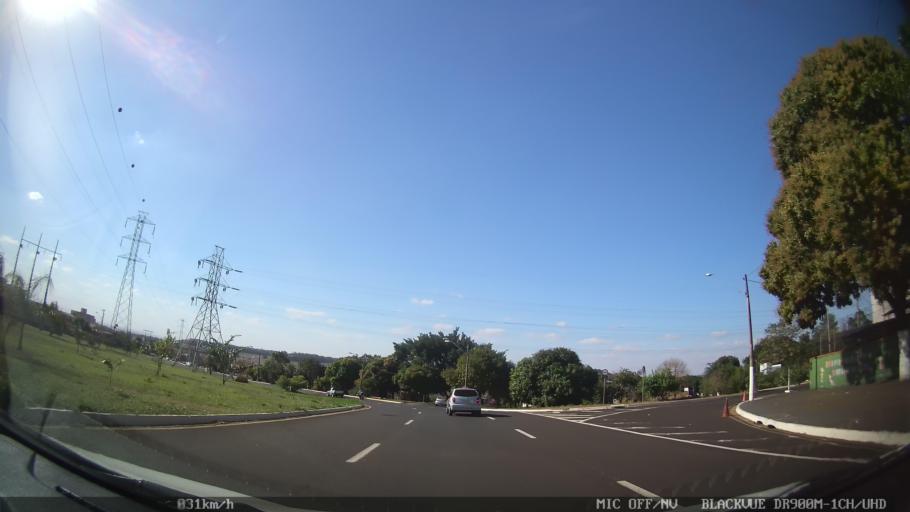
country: BR
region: Sao Paulo
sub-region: Ribeirao Preto
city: Ribeirao Preto
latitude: -21.1858
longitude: -47.7833
